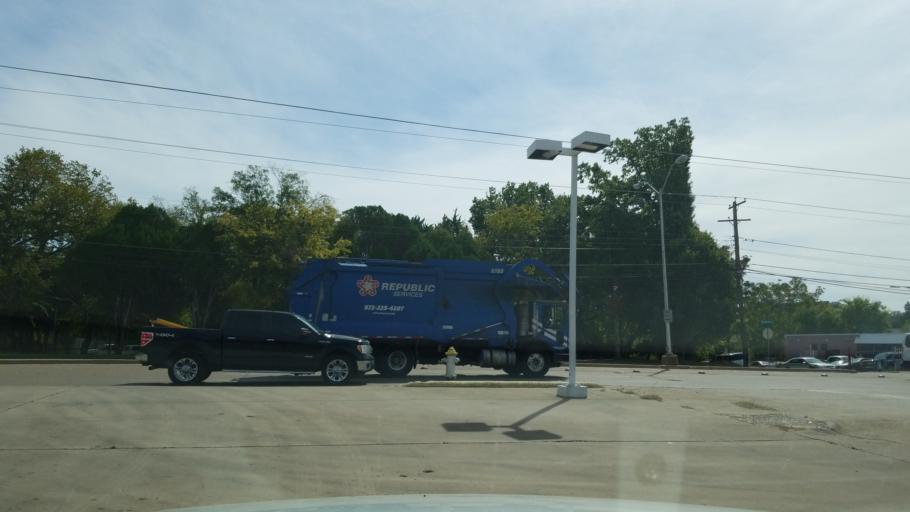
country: US
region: Texas
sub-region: Dallas County
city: Highland Park
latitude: 32.7970
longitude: -96.7203
